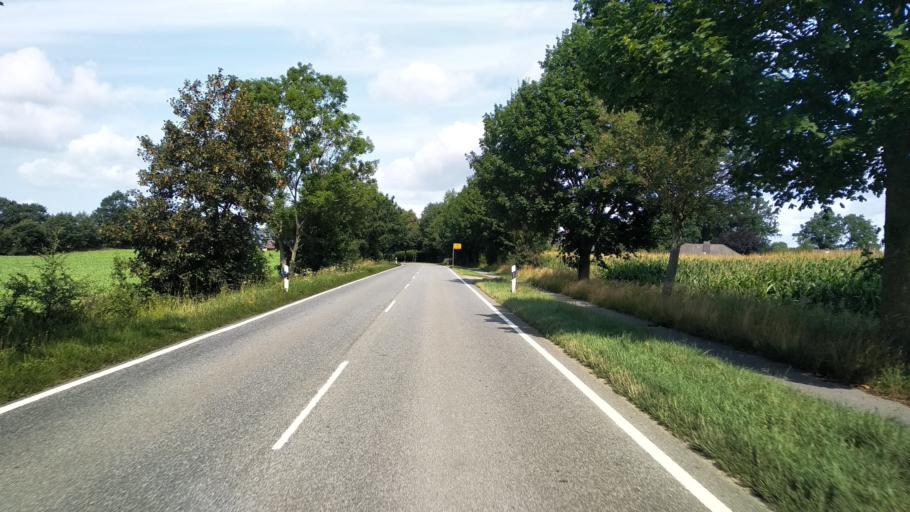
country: DE
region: Schleswig-Holstein
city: Selk
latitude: 54.4682
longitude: 9.5729
